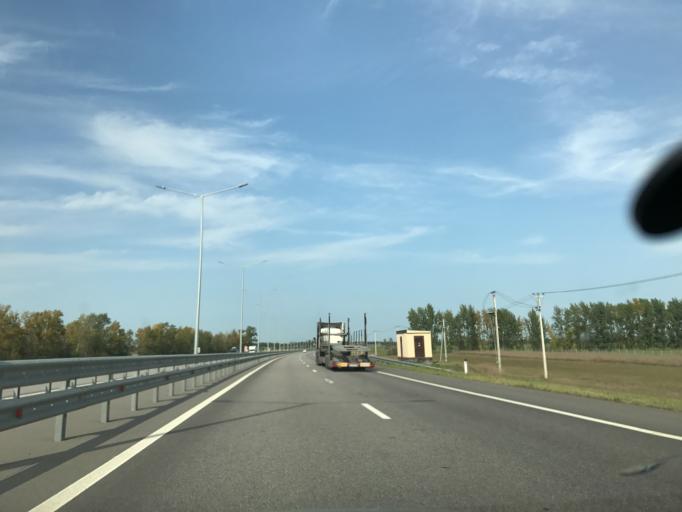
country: RU
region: Voronezj
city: Podkletnoye
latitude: 51.5125
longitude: 39.5132
